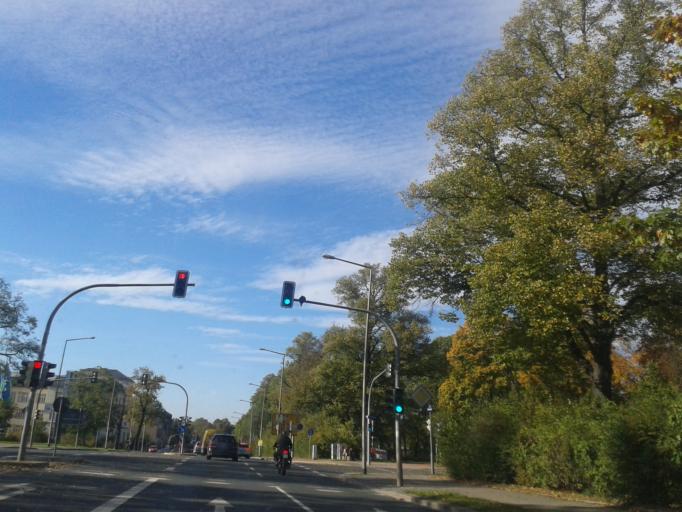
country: DE
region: Saxony
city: Albertstadt
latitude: 51.0757
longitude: 13.7585
